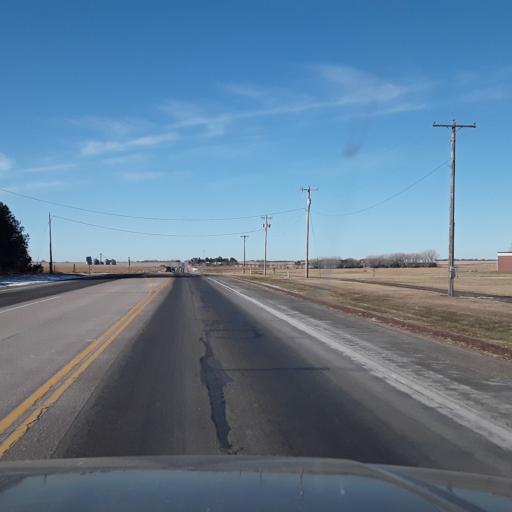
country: US
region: Nebraska
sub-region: Adams County
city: Hastings
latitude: 40.5682
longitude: -98.4589
